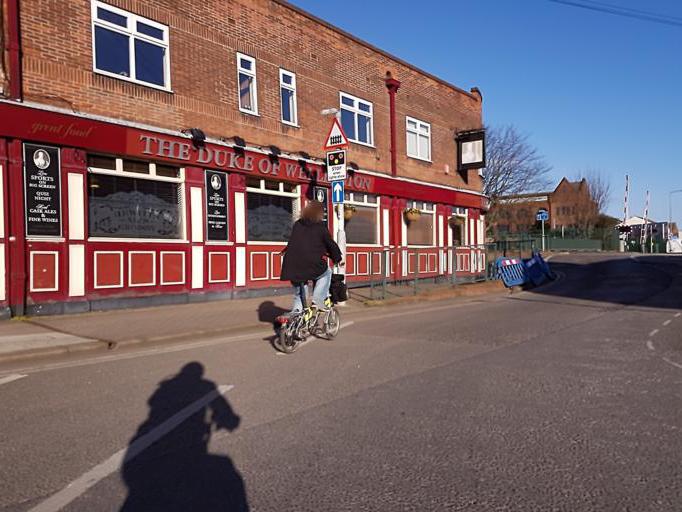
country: GB
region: England
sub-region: North East Lincolnshire
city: Grimsby
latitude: 53.5660
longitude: -0.0807
